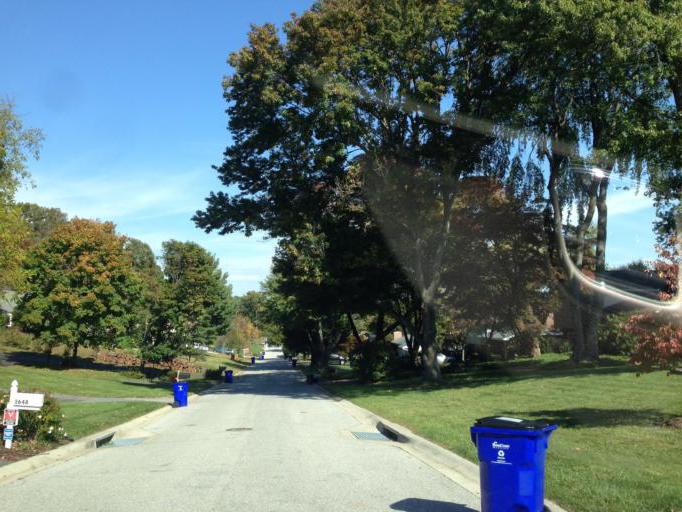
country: US
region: Maryland
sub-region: Howard County
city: Ellicott City
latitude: 39.2690
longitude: -76.8285
